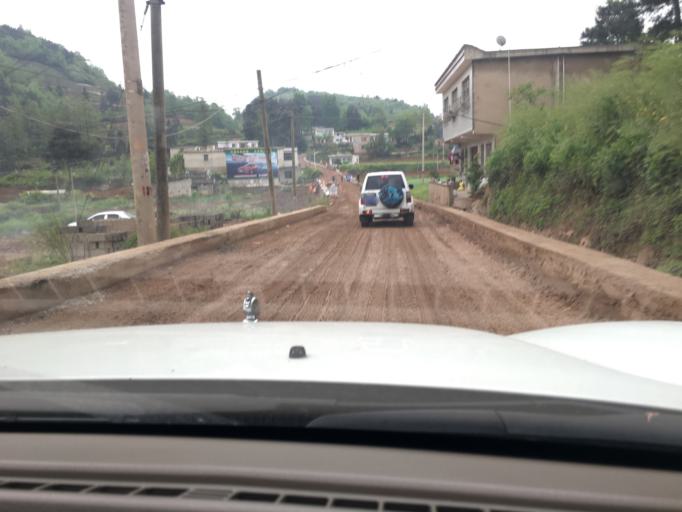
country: CN
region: Guizhou Sheng
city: Supu
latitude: 26.7327
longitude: 106.4371
